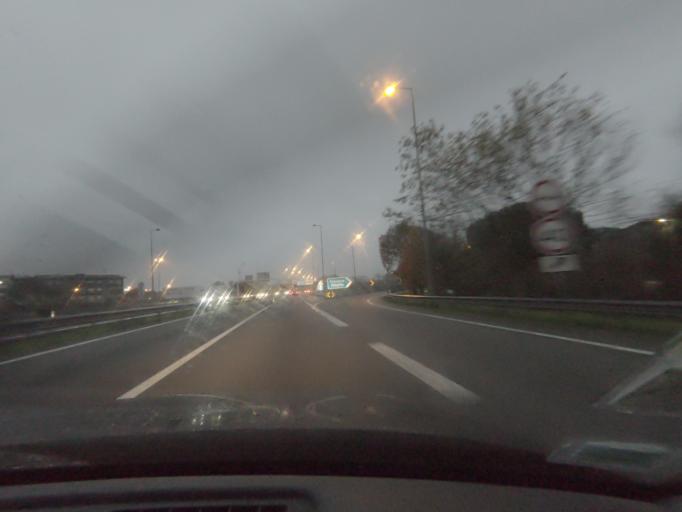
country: PT
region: Porto
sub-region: Matosinhos
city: Santa Cruz do Bispo
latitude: 41.2199
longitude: -8.6915
